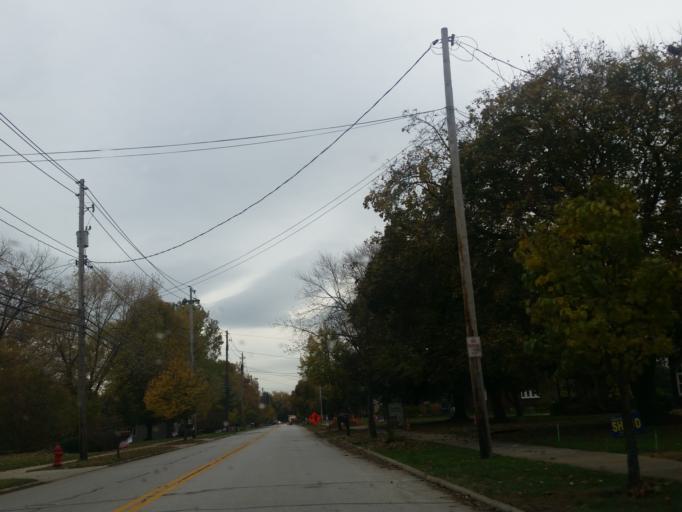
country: US
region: Ohio
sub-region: Cuyahoga County
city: Brooklyn Heights
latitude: 41.4191
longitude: -81.6727
